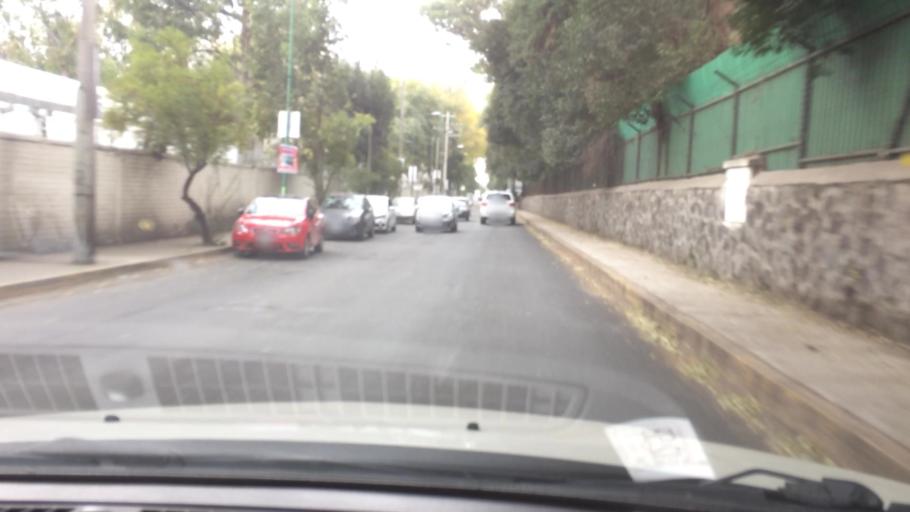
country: MX
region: Mexico City
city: Tlalpan
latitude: 19.2847
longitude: -99.1524
